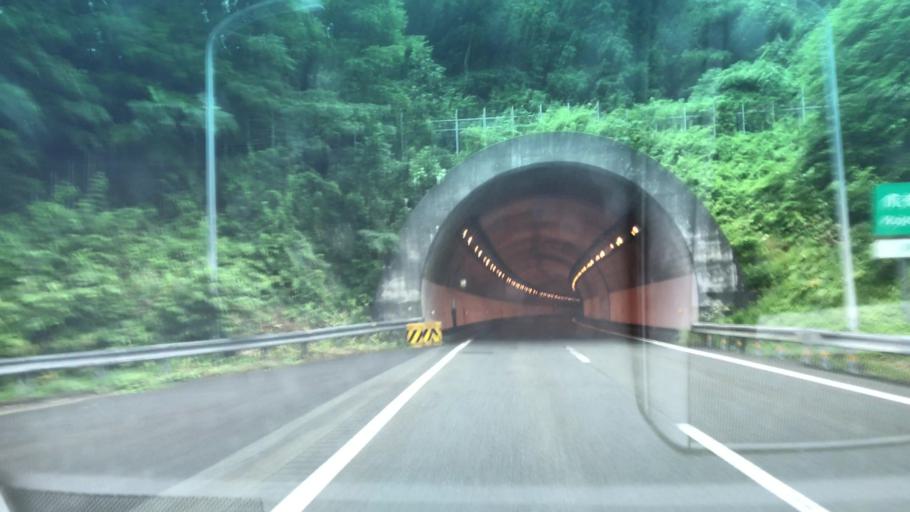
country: JP
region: Hokkaido
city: Shiraoi
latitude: 42.4752
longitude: 141.2174
